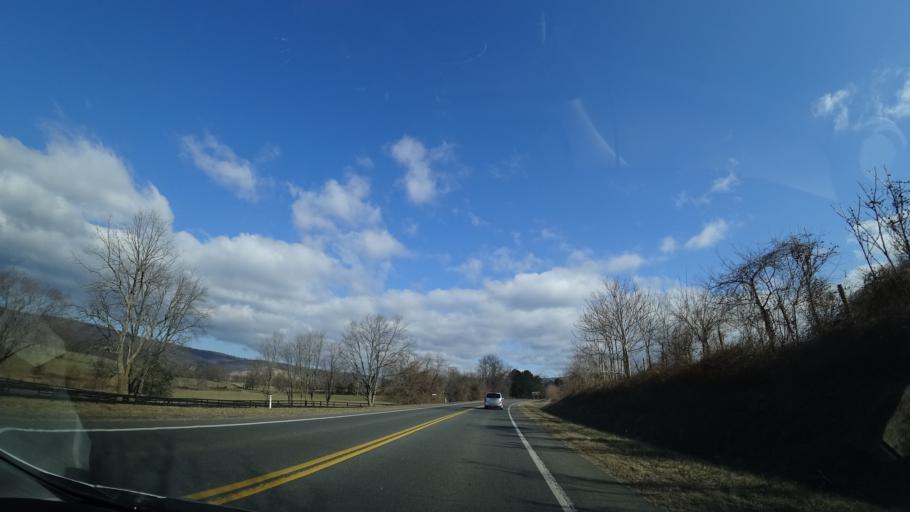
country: US
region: Virginia
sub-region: Warren County
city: Shenandoah Farms
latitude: 38.9737
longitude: -77.9529
